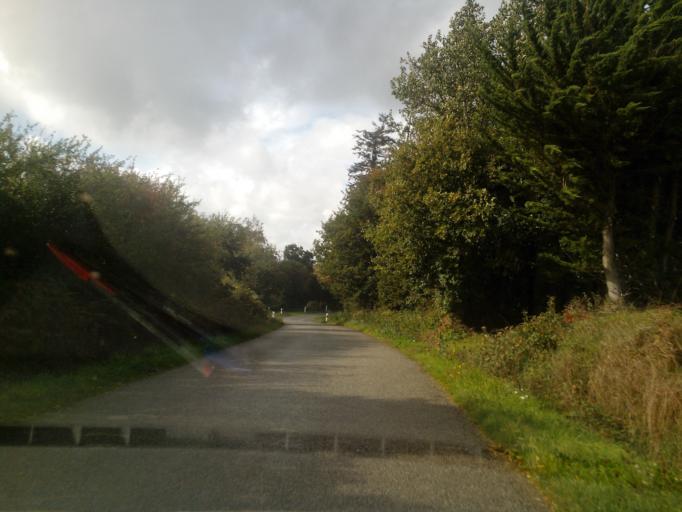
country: FR
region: Brittany
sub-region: Departement du Morbihan
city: Guilliers
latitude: 48.0811
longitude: -2.3563
